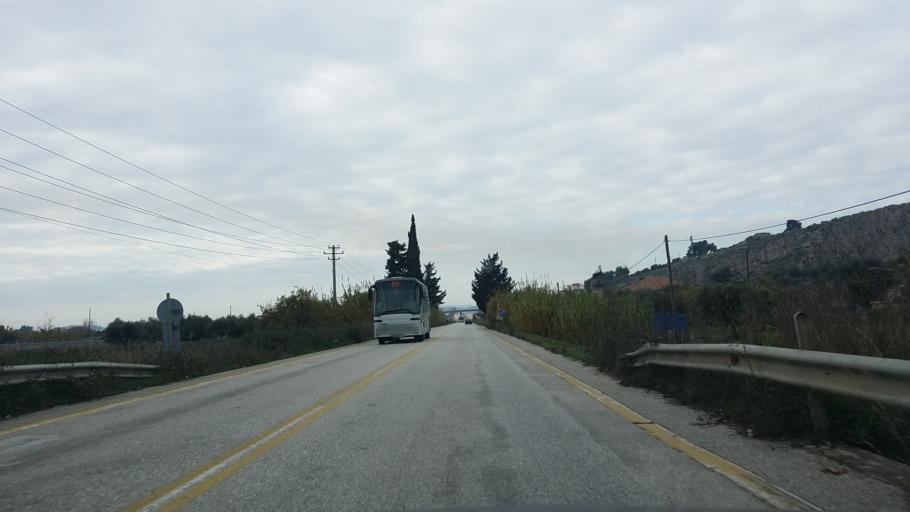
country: GR
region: West Greece
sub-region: Nomos Aitolias kai Akarnanias
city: Mesolongi
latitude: 38.3955
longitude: 21.4224
